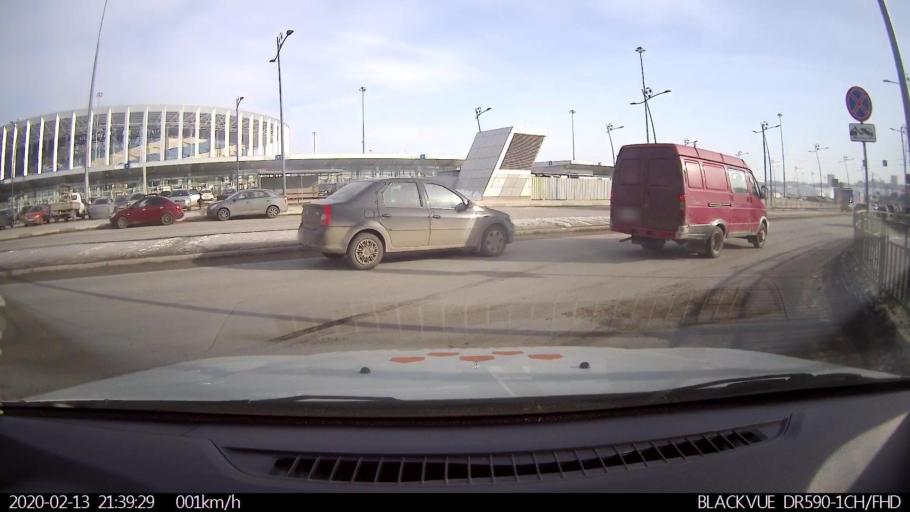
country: RU
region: Nizjnij Novgorod
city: Nizhniy Novgorod
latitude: 56.3370
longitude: 43.9639
